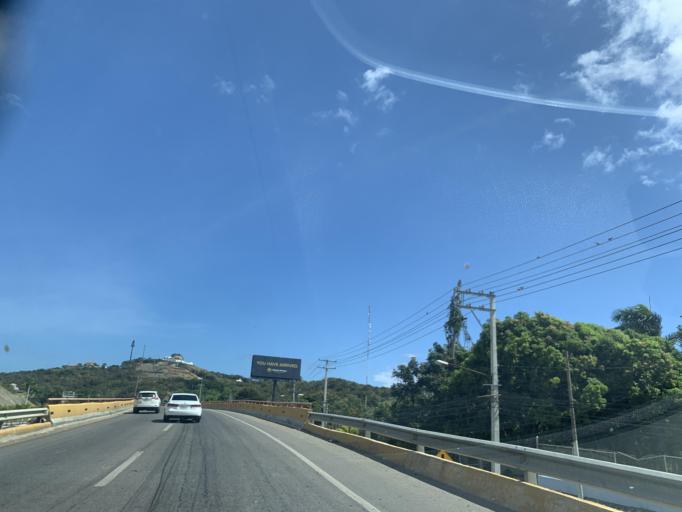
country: DO
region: Puerto Plata
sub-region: Puerto Plata
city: Puerto Plata
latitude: 19.8163
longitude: -70.7325
